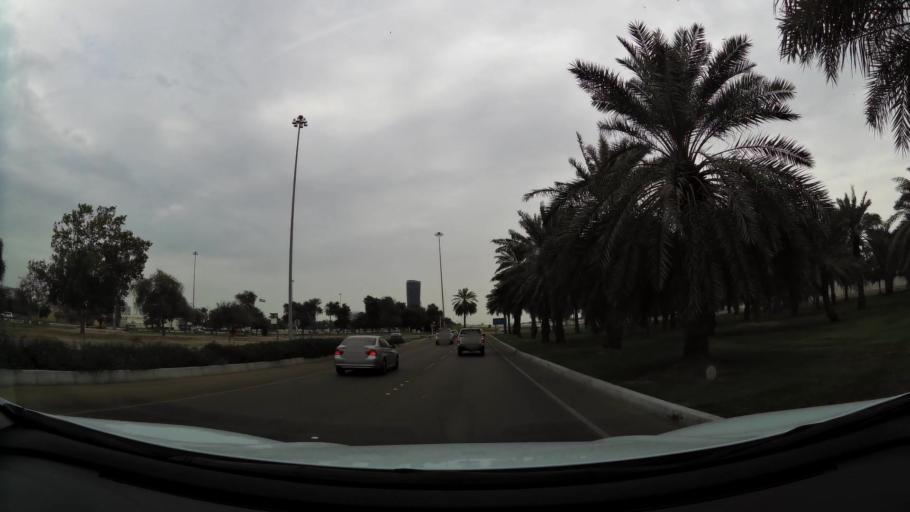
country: AE
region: Abu Dhabi
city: Abu Dhabi
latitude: 24.4209
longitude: 54.4197
